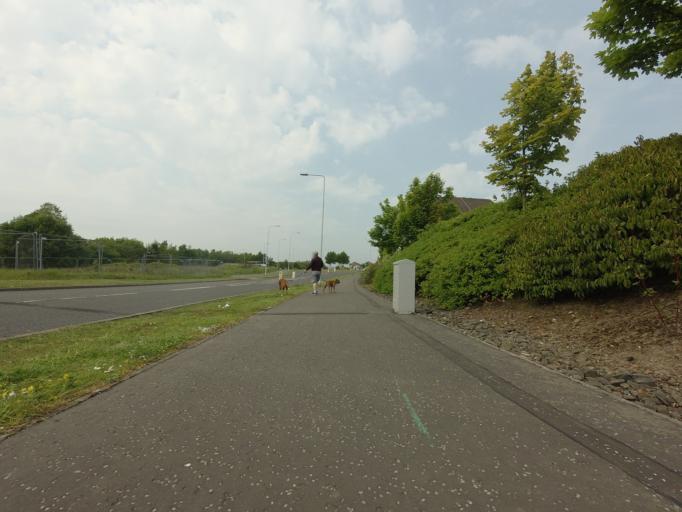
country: GB
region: Scotland
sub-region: Fife
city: Inverkeithing
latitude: 56.0504
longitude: -3.4111
